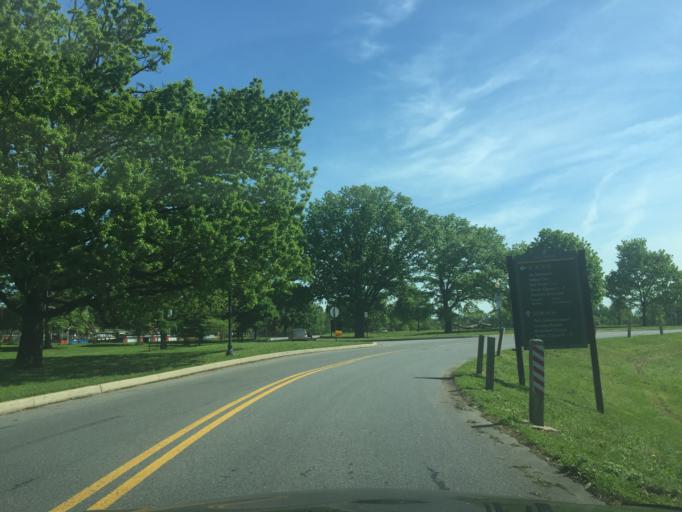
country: US
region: Maryland
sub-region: City of Baltimore
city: Baltimore
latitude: 39.3203
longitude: -76.6386
